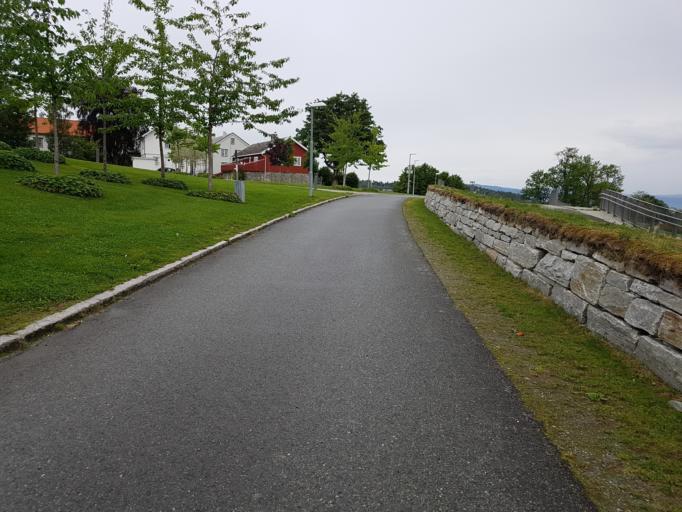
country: NO
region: Sor-Trondelag
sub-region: Trondheim
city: Trondheim
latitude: 63.4049
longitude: 10.3714
